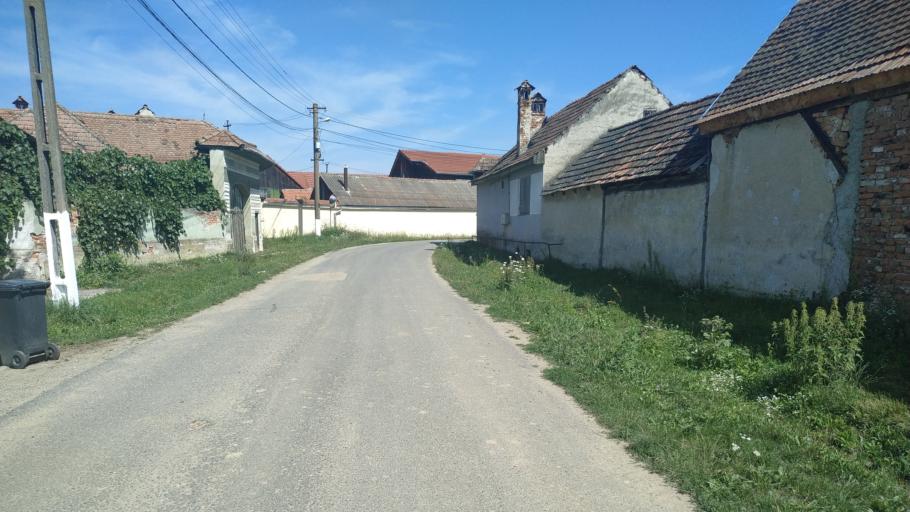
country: RO
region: Brasov
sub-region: Comuna Beclean
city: Beclean
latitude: 45.8261
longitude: 24.9263
